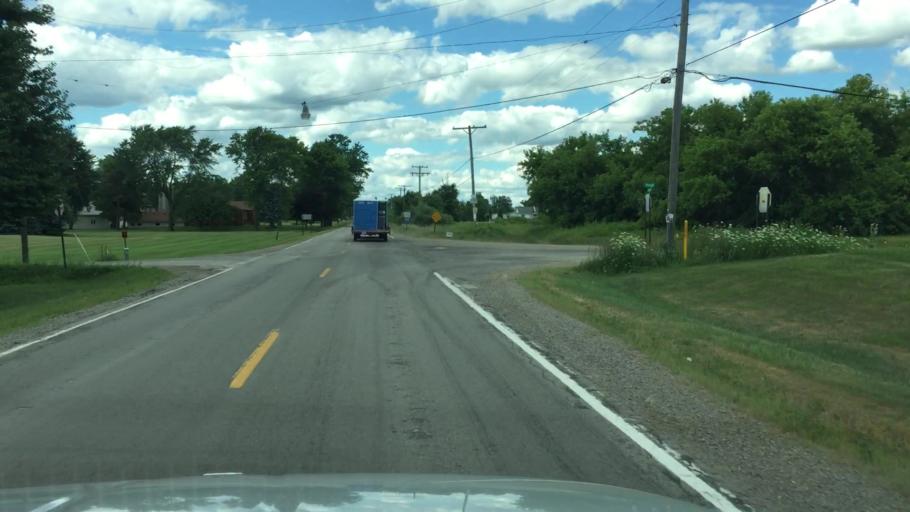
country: US
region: Michigan
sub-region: Macomb County
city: Armada
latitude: 42.9087
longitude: -82.9454
